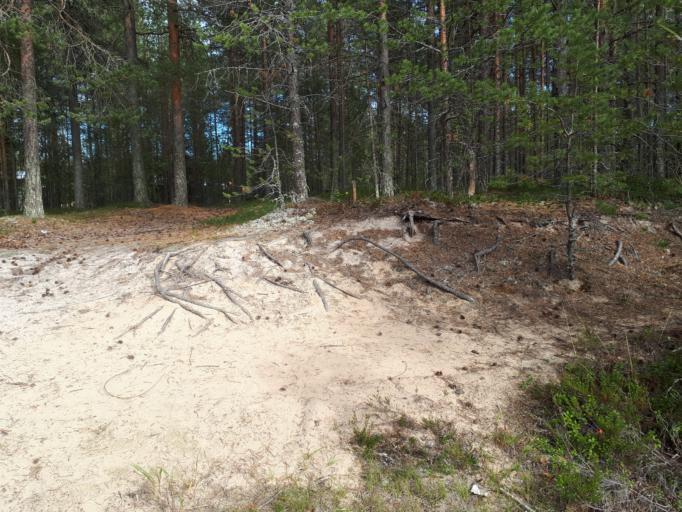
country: FI
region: Northern Ostrobothnia
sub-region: Oulunkaari
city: Ii
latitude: 65.2899
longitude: 25.3807
